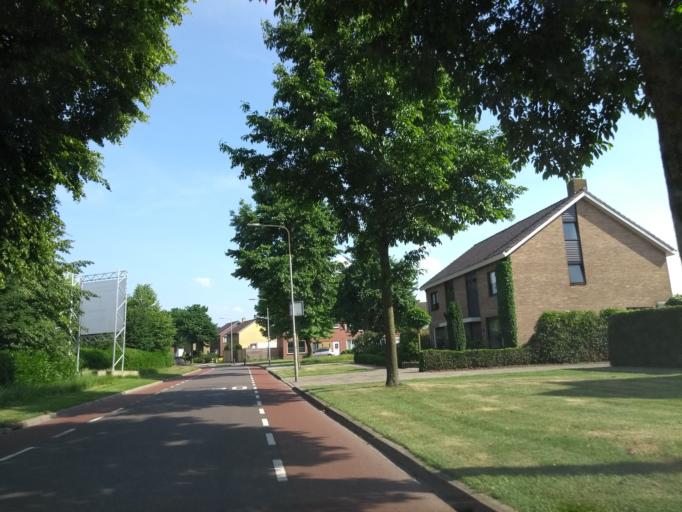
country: DE
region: Lower Saxony
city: Nordhorn
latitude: 52.3785
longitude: 7.0053
